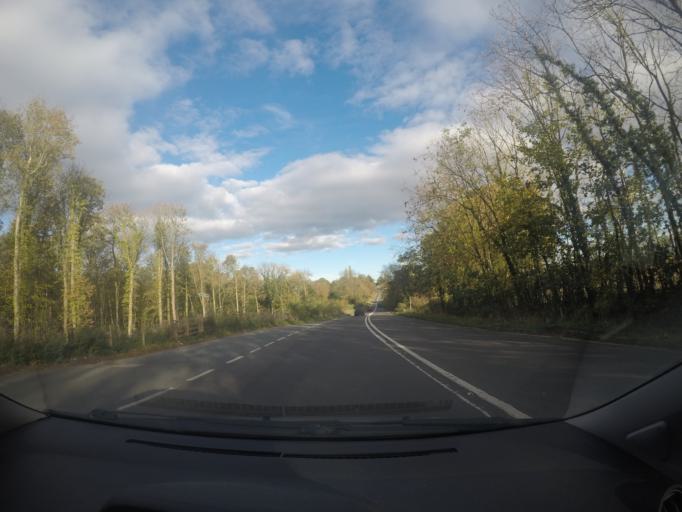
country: GB
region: England
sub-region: City and Borough of Leeds
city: Thorner
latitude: 53.8477
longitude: -1.4079
